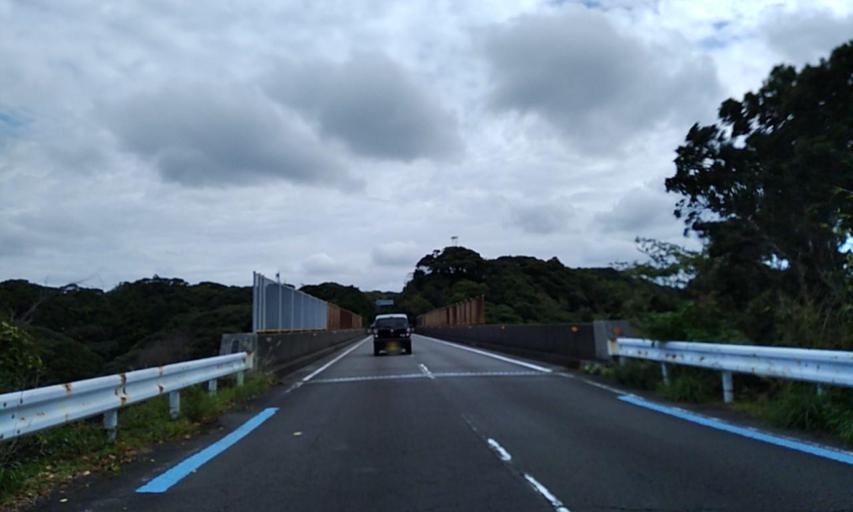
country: JP
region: Wakayama
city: Shingu
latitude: 33.4690
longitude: 135.8517
